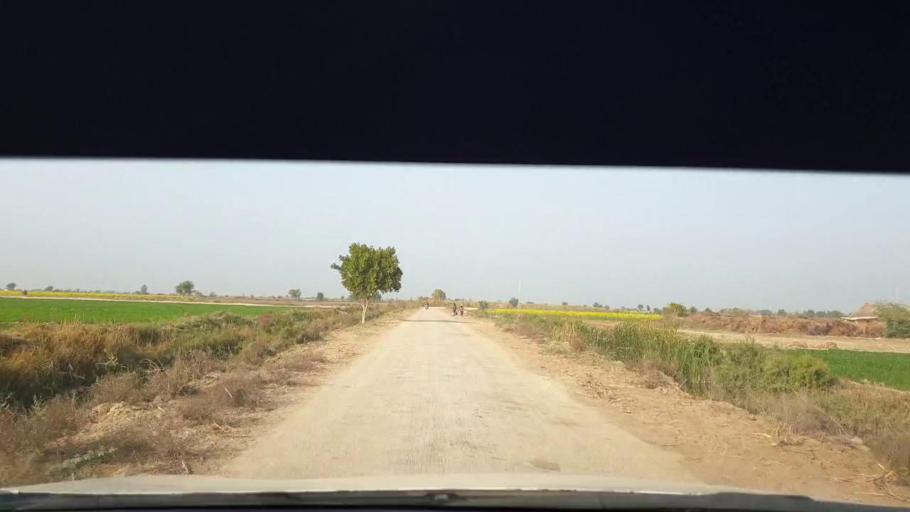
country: PK
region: Sindh
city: Berani
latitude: 25.7584
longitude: 68.9405
